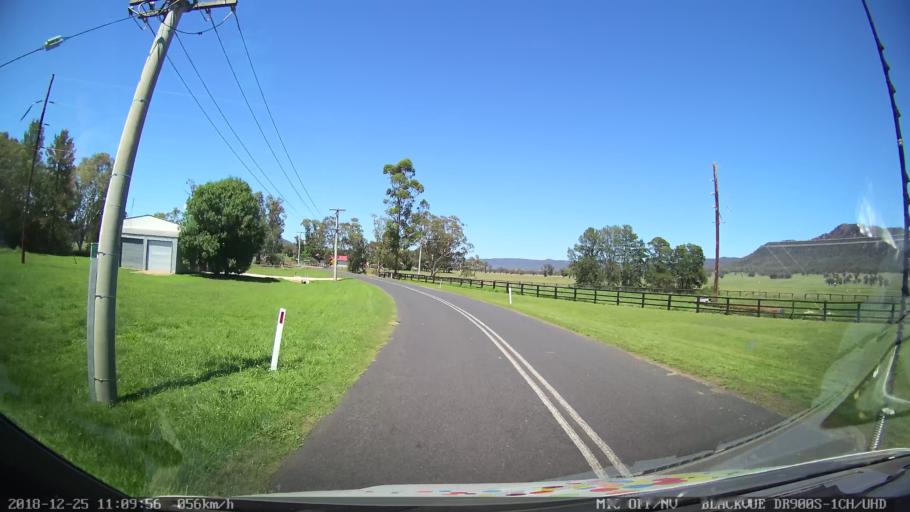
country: AU
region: New South Wales
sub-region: Upper Hunter Shire
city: Merriwa
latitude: -32.4143
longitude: 150.1163
